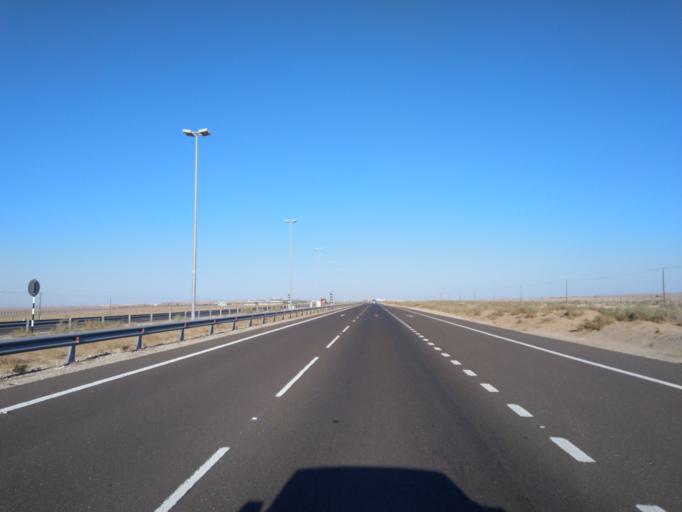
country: OM
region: Al Buraimi
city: Al Buraymi
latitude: 24.4980
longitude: 55.4328
